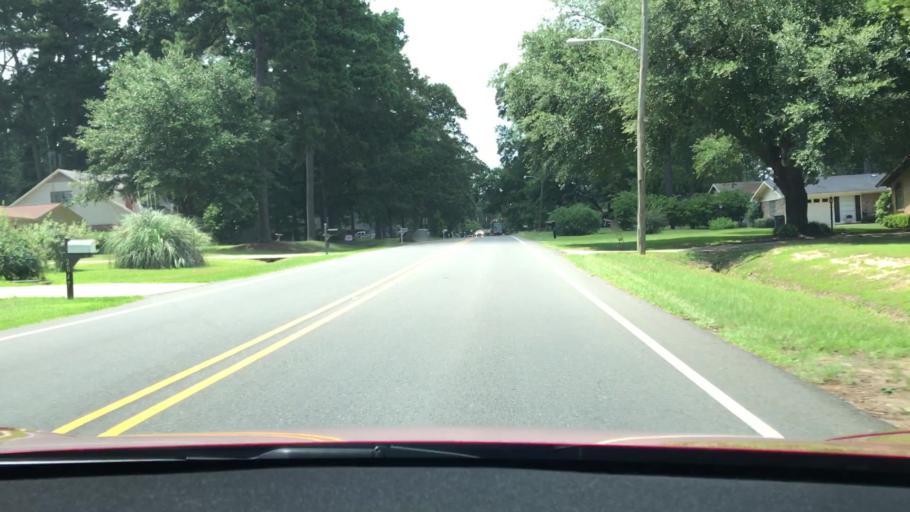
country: US
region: Louisiana
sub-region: De Soto Parish
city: Stonewall
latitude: 32.3900
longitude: -93.7935
